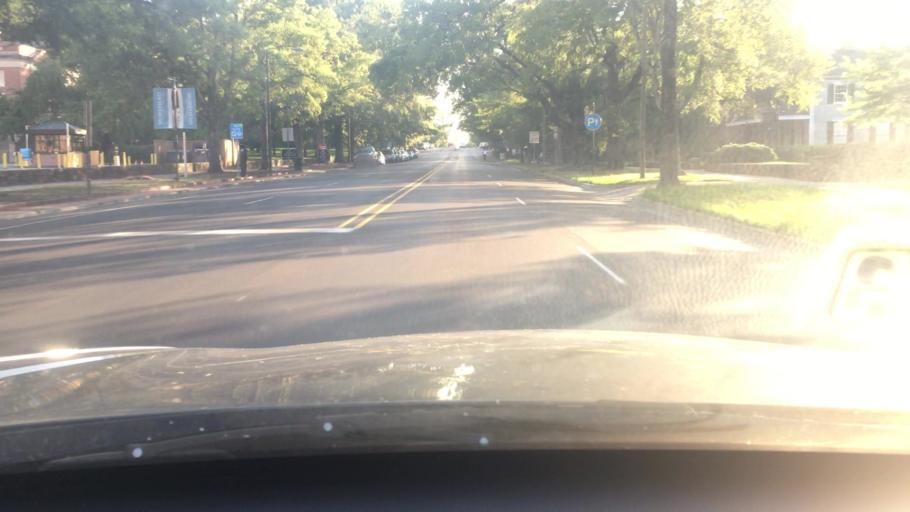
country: US
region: North Carolina
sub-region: Orange County
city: Chapel Hill
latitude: 35.9151
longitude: -79.0509
